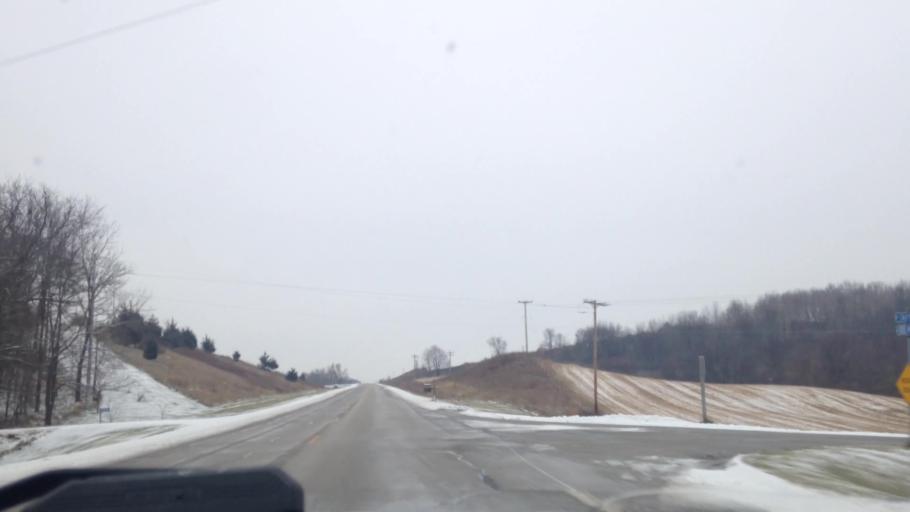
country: US
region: Wisconsin
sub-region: Dodge County
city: Hustisford
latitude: 43.2794
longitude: -88.5185
